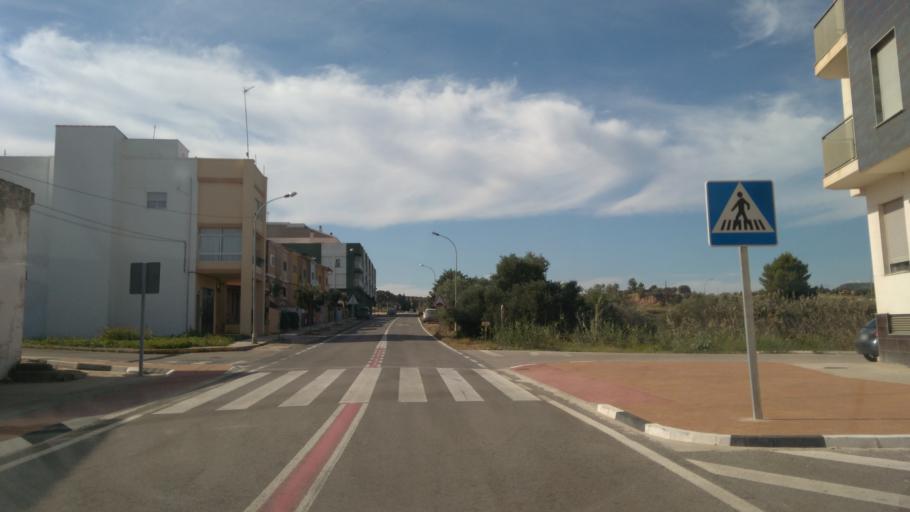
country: ES
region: Valencia
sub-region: Provincia de Valencia
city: Montroy
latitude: 39.3430
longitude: -0.6148
